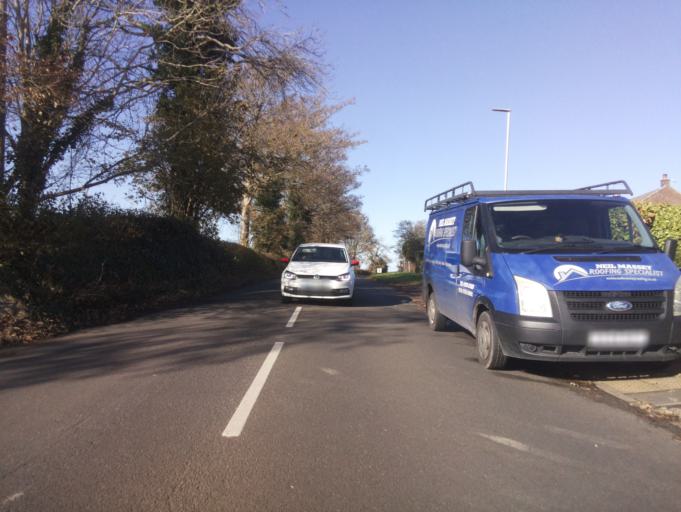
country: GB
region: England
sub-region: Somerset
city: Yeovil
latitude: 50.9549
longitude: -2.6493
